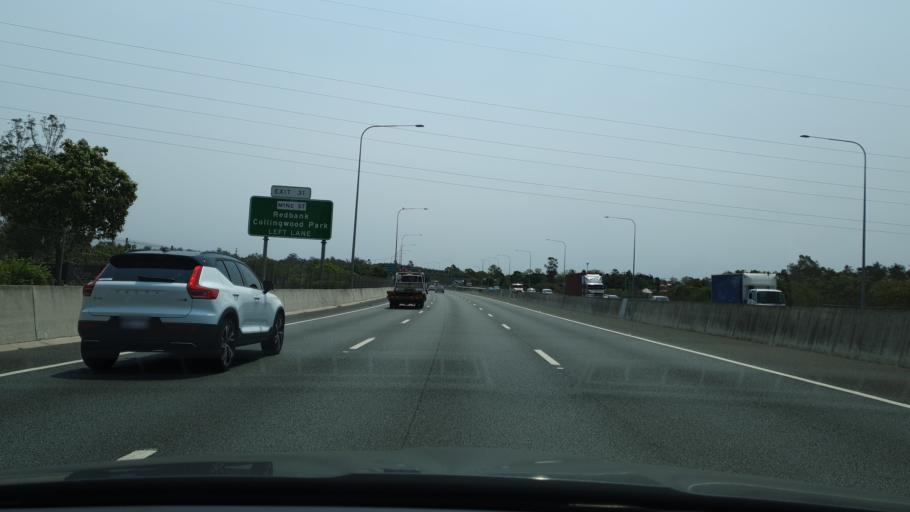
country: AU
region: Queensland
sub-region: Ipswich
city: Redbank
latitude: -27.6013
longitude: 152.8810
